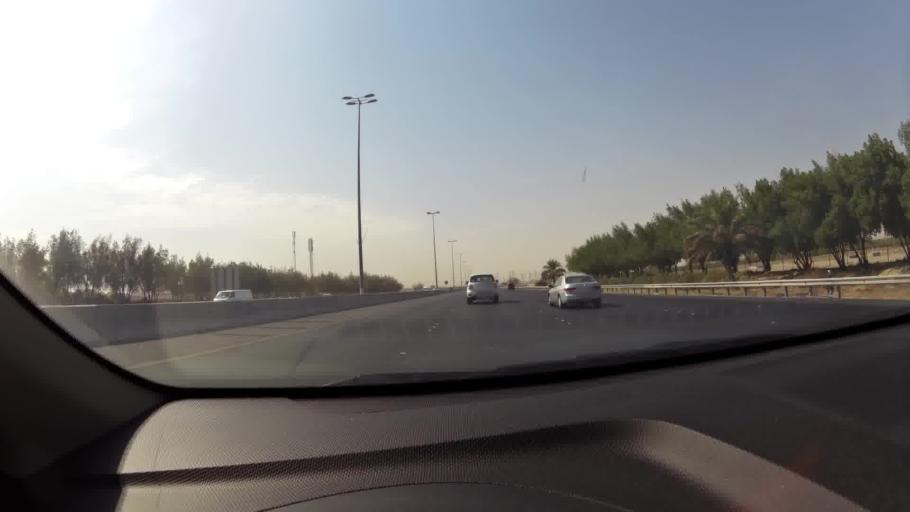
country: KW
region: Mubarak al Kabir
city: Mubarak al Kabir
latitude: 29.1860
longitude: 48.0655
